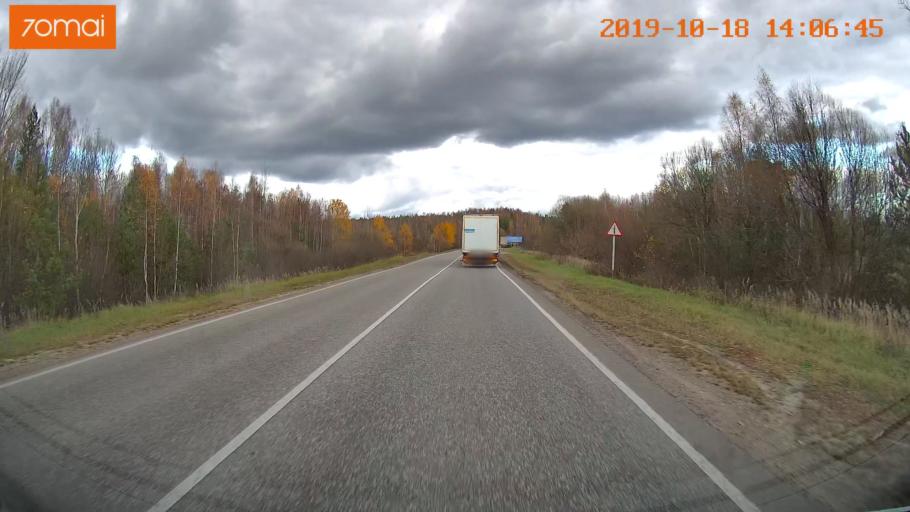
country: RU
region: Rjazan
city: Spas-Klepiki
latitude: 55.1485
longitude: 40.1528
